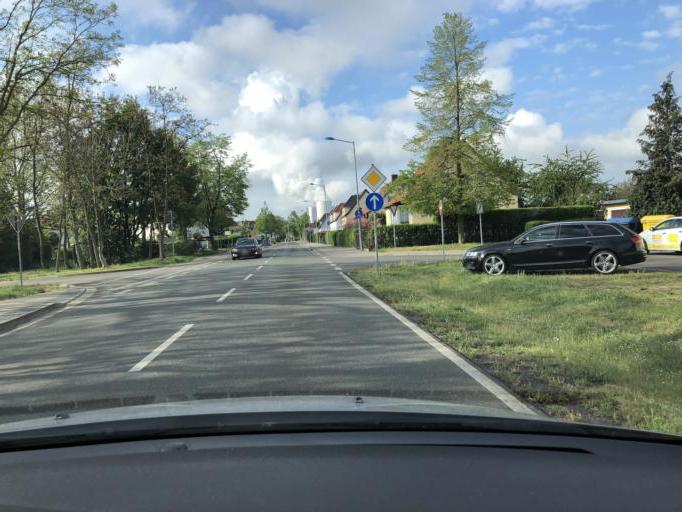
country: DE
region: Saxony
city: Bohlen
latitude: 51.2077
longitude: 12.3857
